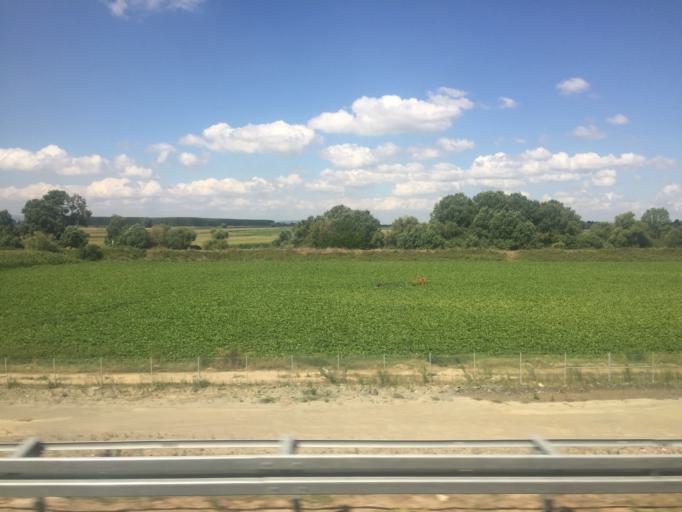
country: TR
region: Bursa
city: Tatkavakli
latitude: 40.1001
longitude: 28.2784
